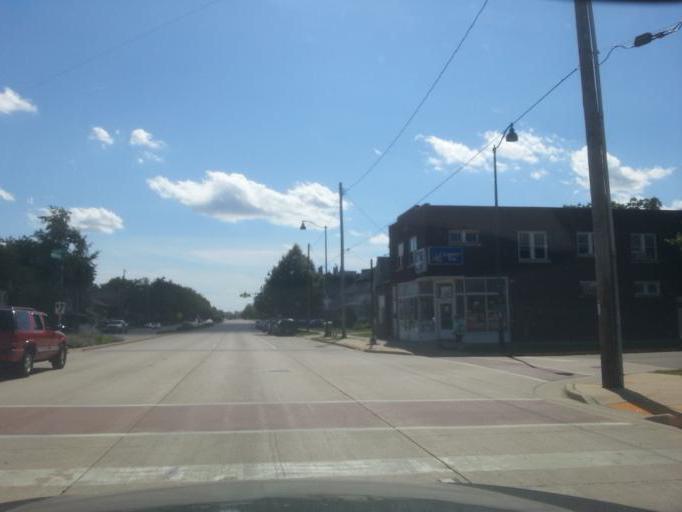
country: US
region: Wisconsin
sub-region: Dane County
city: Maple Bluff
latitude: 43.0986
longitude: -89.3509
